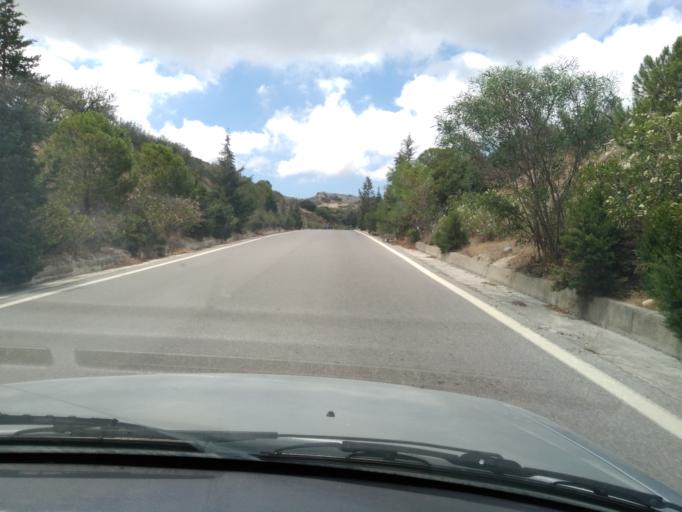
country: GR
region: Crete
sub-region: Nomos Lasithiou
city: Makry-Gialos
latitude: 35.0672
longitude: 26.0470
